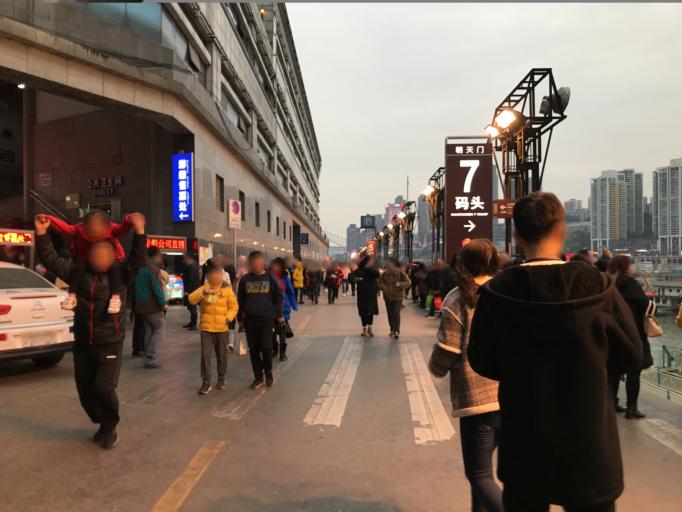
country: CN
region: Chongqing Shi
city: Nanping
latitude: 29.5688
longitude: 106.5851
